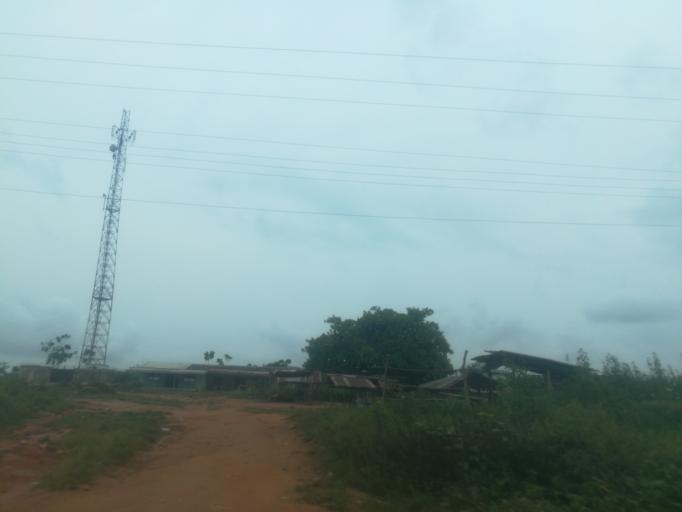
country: NG
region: Ogun
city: Ayetoro
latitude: 7.1072
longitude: 3.1384
